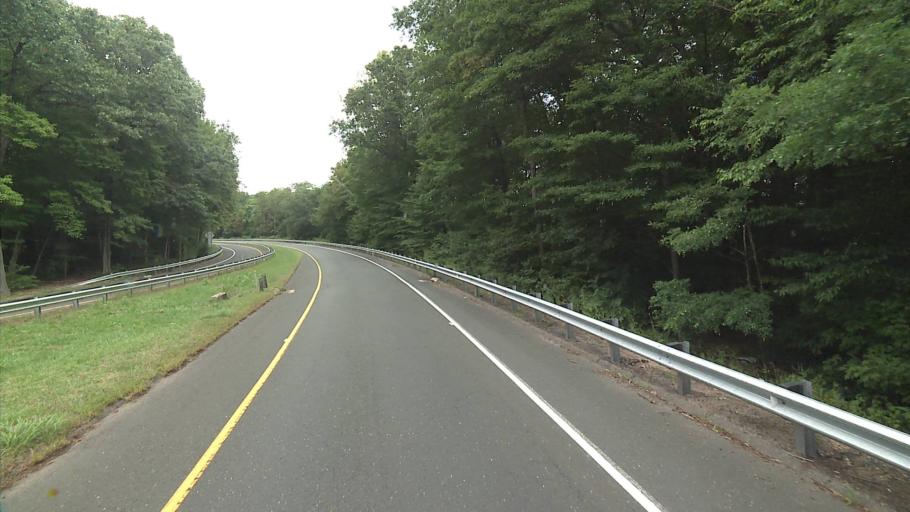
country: US
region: Connecticut
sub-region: Hartford County
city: Tariffville
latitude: 41.8933
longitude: -72.7488
